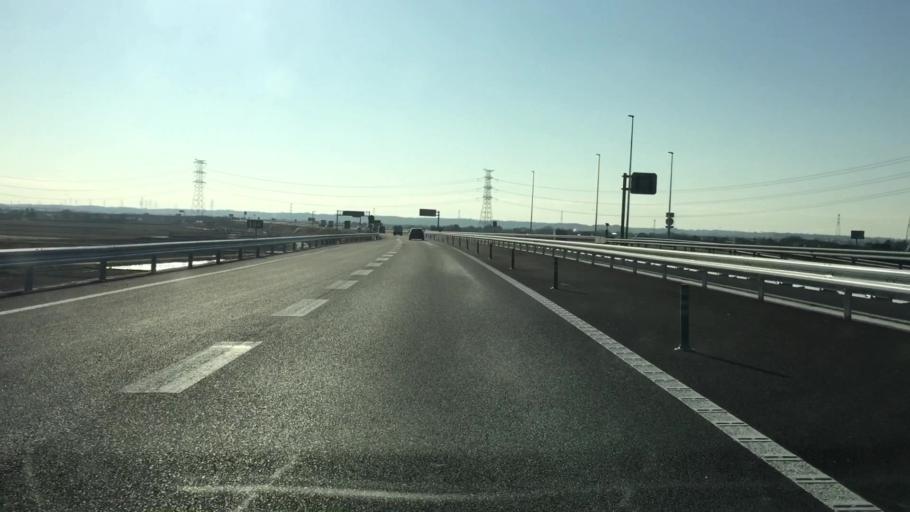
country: JP
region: Ibaraki
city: Inashiki
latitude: 35.9235
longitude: 140.3479
